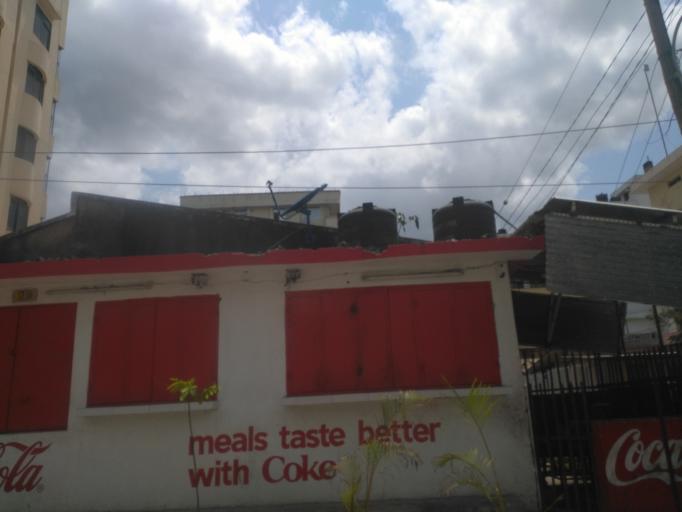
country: TZ
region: Dar es Salaam
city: Dar es Salaam
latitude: -6.8157
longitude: 39.2722
